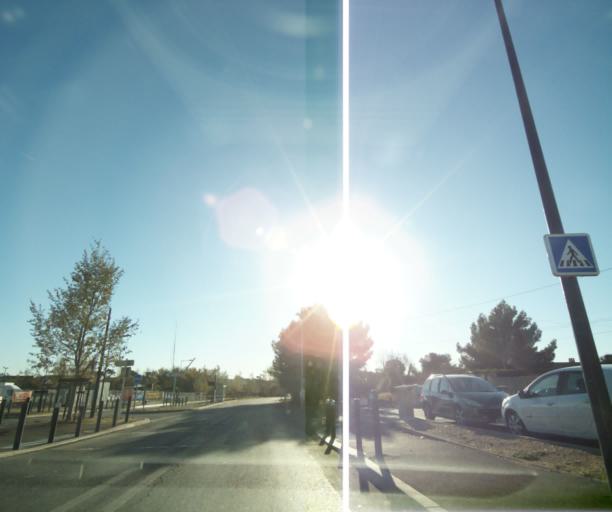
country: FR
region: Provence-Alpes-Cote d'Azur
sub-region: Departement des Bouches-du-Rhone
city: Plan-de-Cuques
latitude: 43.3462
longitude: 5.4487
